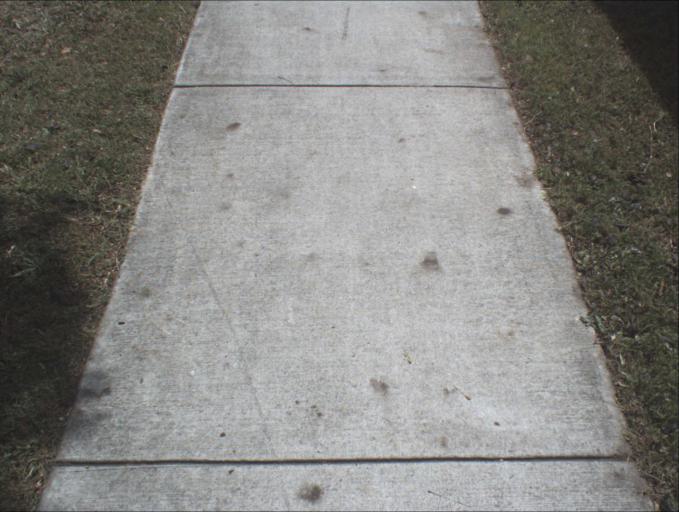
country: AU
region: Queensland
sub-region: Logan
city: Slacks Creek
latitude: -27.6604
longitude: 153.1441
